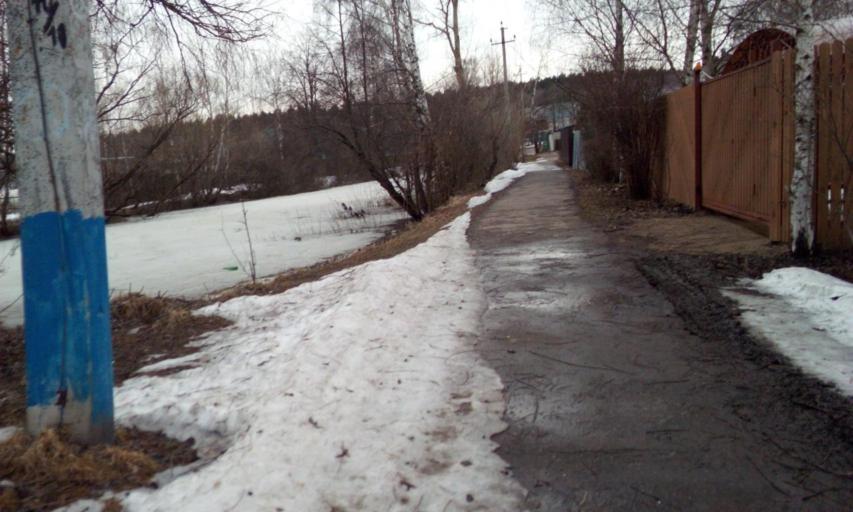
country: RU
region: Moskovskaya
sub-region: Leninskiy Rayon
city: Vnukovo
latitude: 55.6226
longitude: 37.2624
